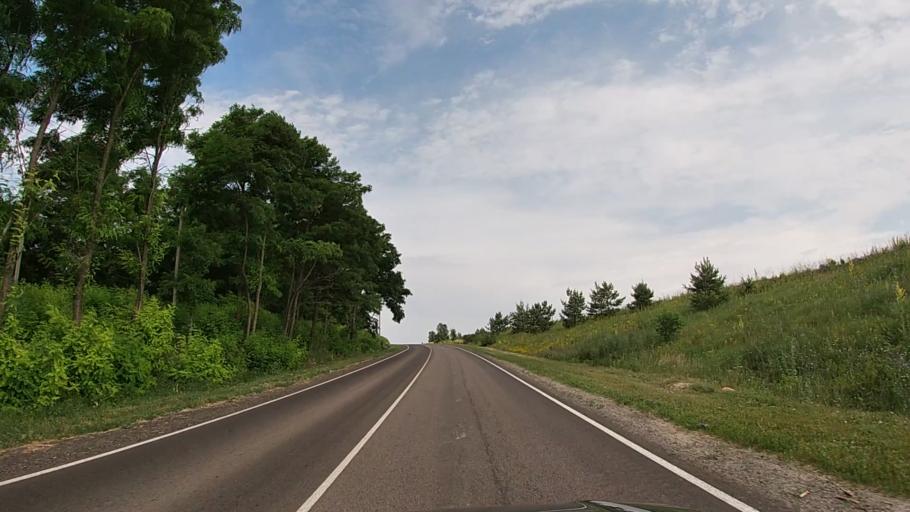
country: RU
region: Belgorod
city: Krasnaya Yaruga
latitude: 50.8299
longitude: 35.4951
